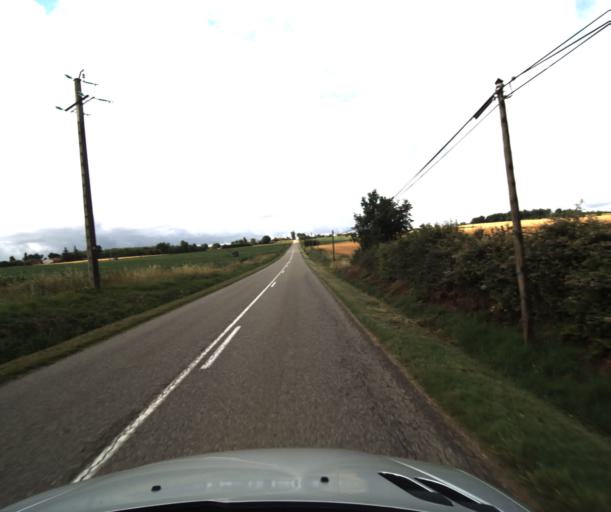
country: FR
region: Midi-Pyrenees
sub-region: Departement du Tarn-et-Garonne
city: Saint-Nicolas-de-la-Grave
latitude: 44.0057
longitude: 0.9910
